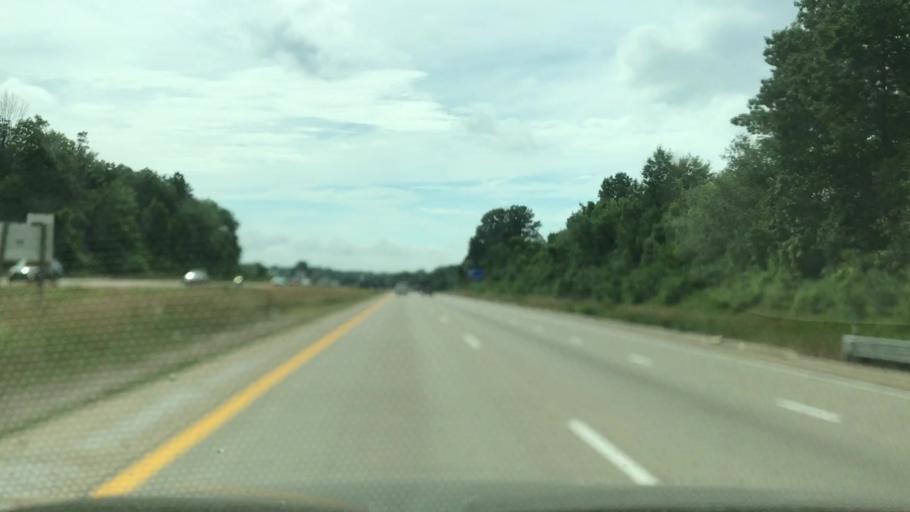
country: US
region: Michigan
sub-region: Kent County
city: Comstock Park
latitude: 43.0206
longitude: -85.7103
